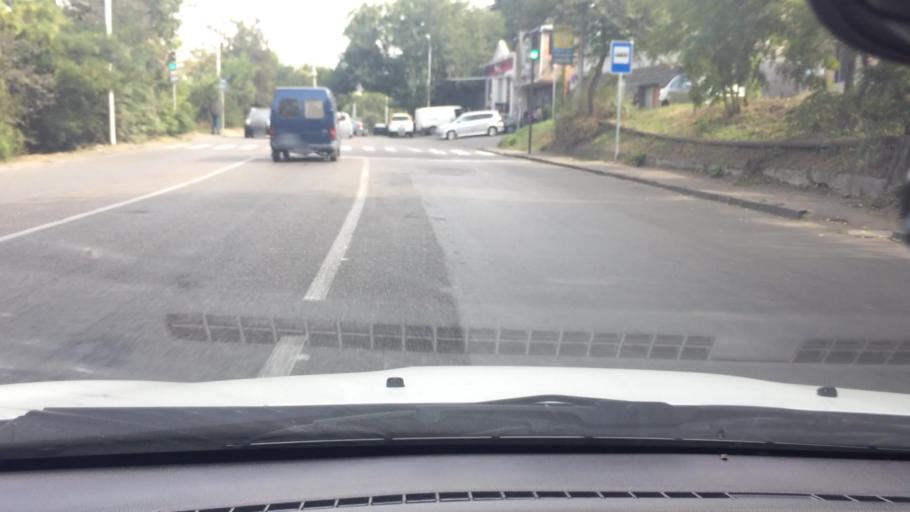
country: GE
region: T'bilisi
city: Tbilisi
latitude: 41.6717
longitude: 44.8364
